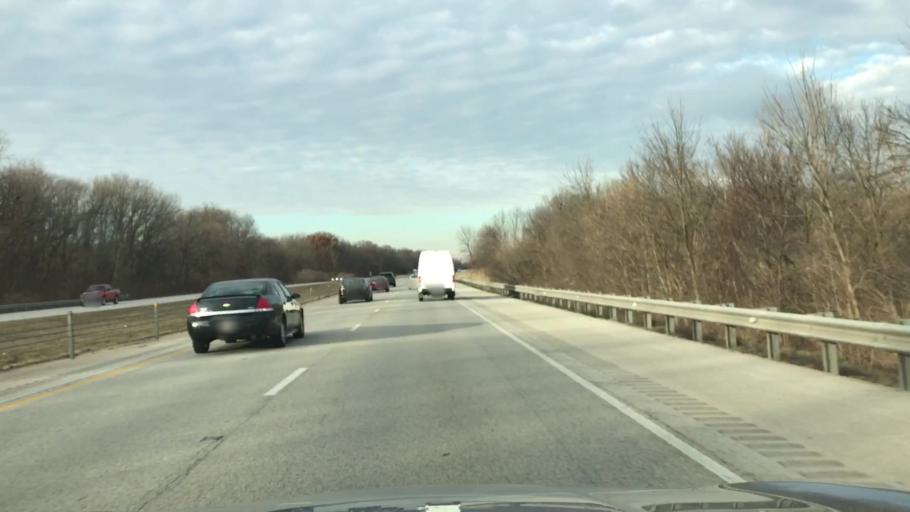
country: US
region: Illinois
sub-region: Sangamon County
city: Sherman
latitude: 39.8746
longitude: -89.5964
